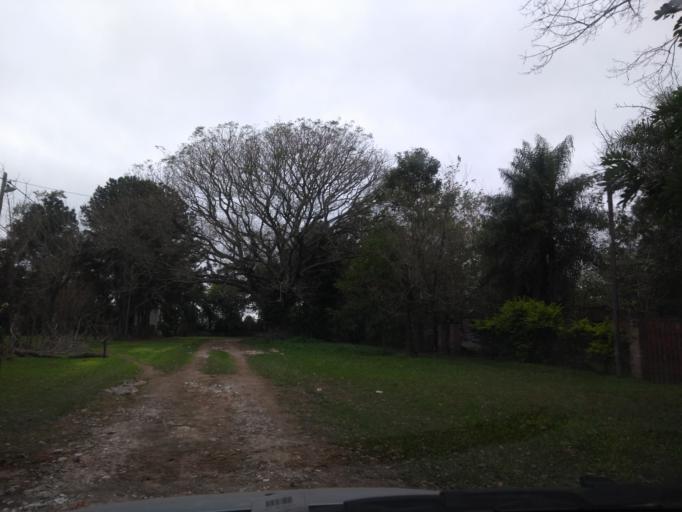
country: AR
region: Chaco
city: Barranqueras
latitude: -27.4260
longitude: -58.9332
